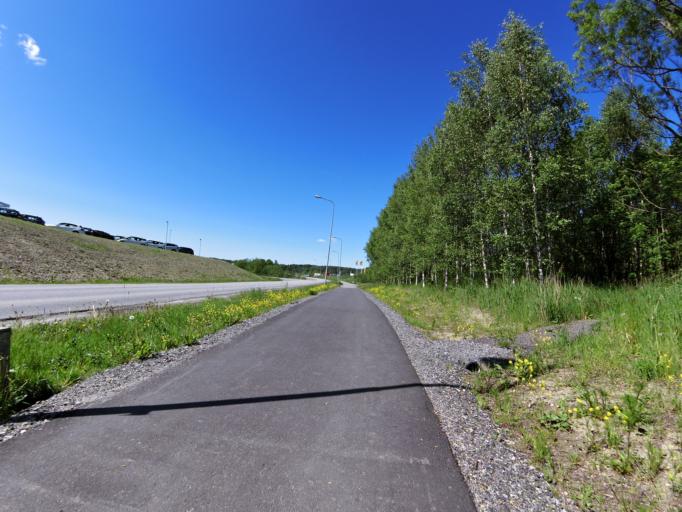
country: NO
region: Ostfold
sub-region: Fredrikstad
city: Fredrikstad
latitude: 59.2410
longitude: 10.9847
